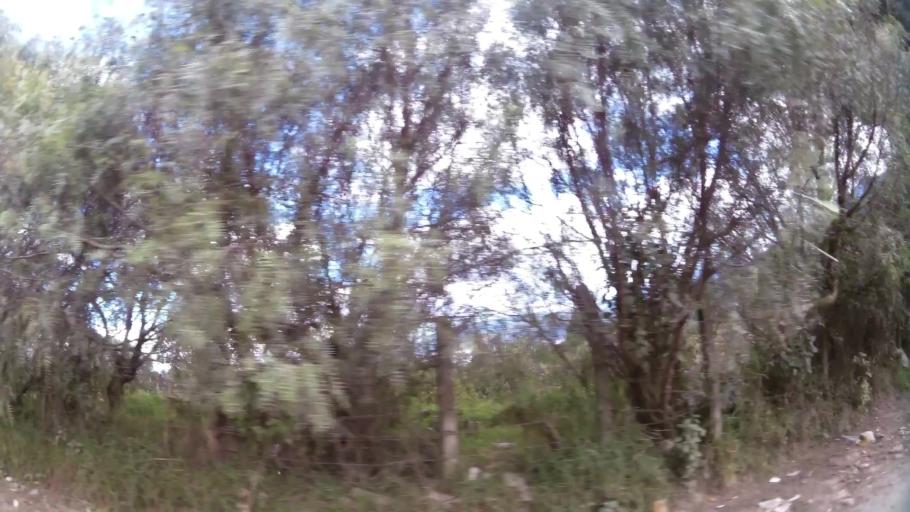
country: GT
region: Quetzaltenango
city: Quetzaltenango
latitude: 14.8409
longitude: -91.5424
